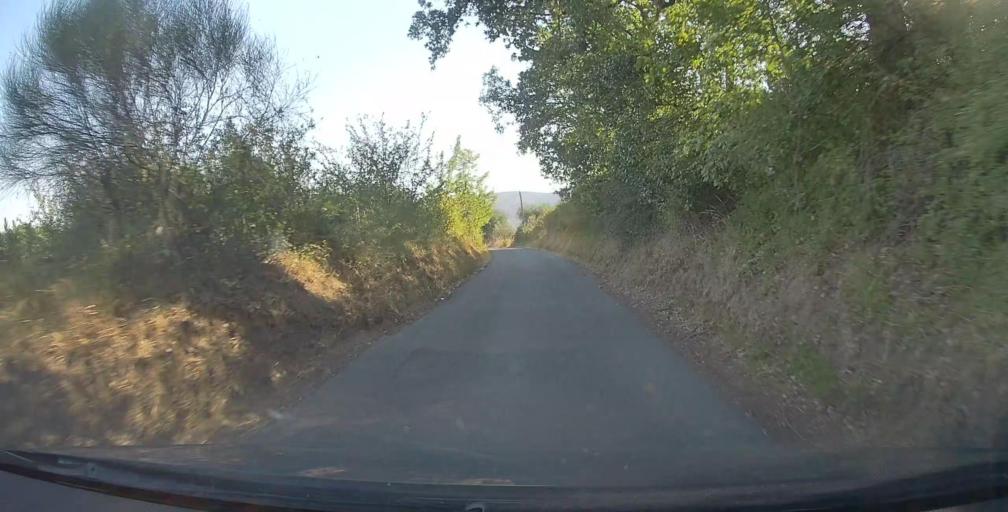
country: IT
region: Umbria
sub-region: Provincia di Terni
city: Calvi dell'Umbria
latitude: 42.3765
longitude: 12.5666
